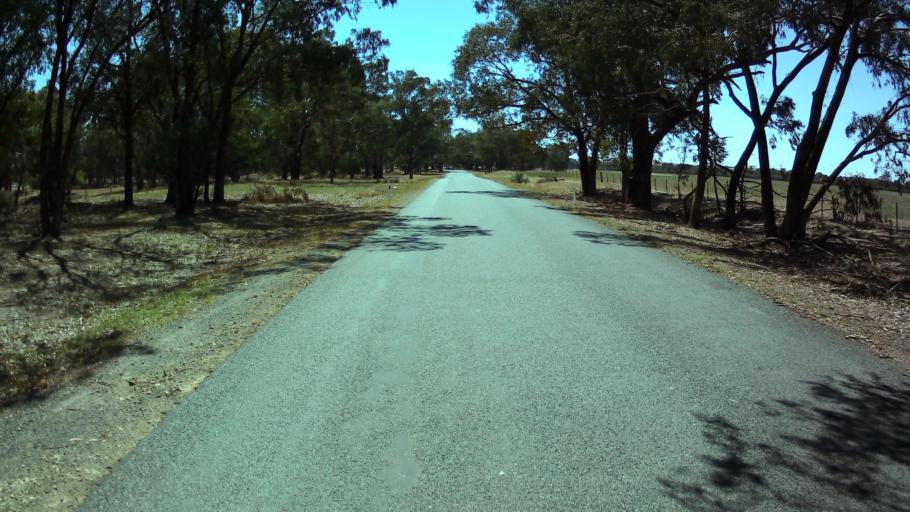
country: AU
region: New South Wales
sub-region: Weddin
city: Grenfell
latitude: -33.9999
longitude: 148.3933
